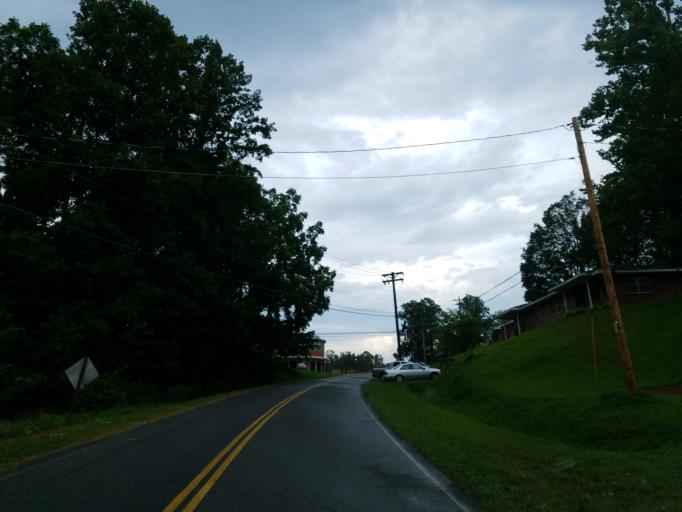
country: US
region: Georgia
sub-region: Fannin County
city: Blue Ridge
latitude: 34.8568
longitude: -84.3314
